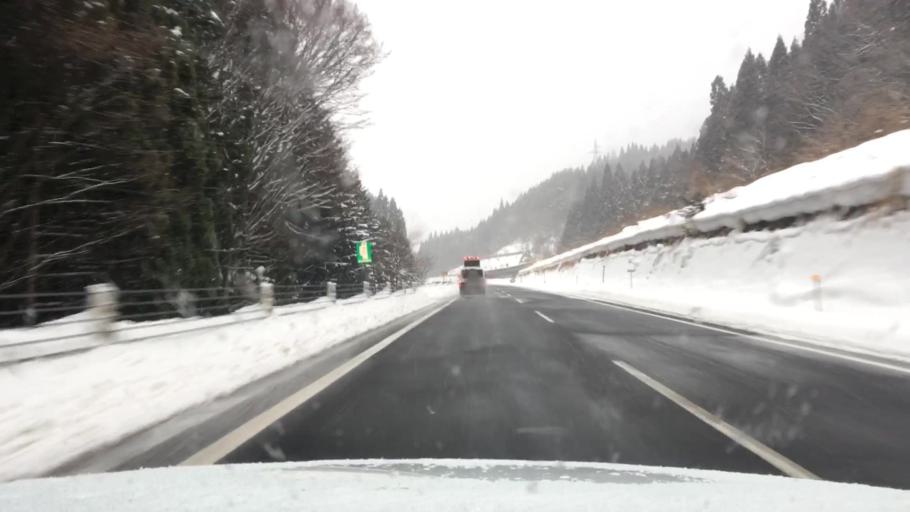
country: JP
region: Akita
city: Hanawa
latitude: 40.1436
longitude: 140.8084
